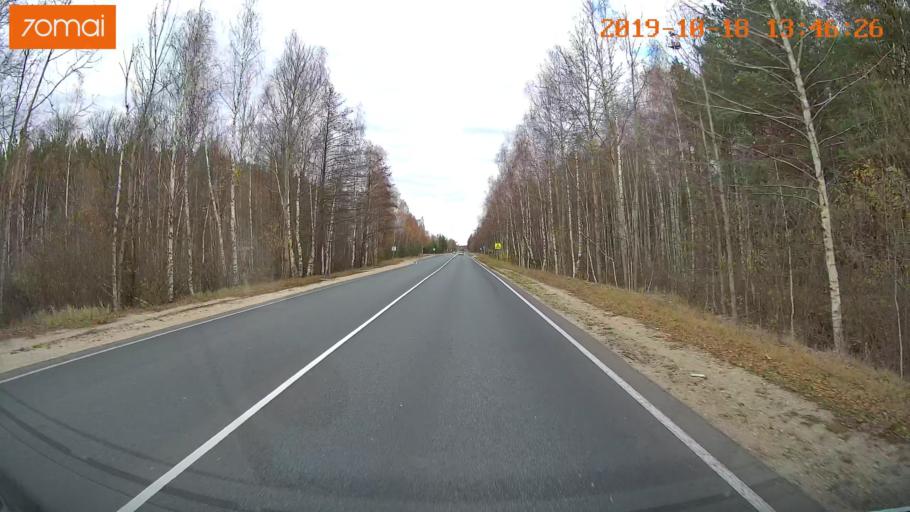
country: RU
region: Rjazan
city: Solotcha
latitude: 54.9610
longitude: 39.9416
